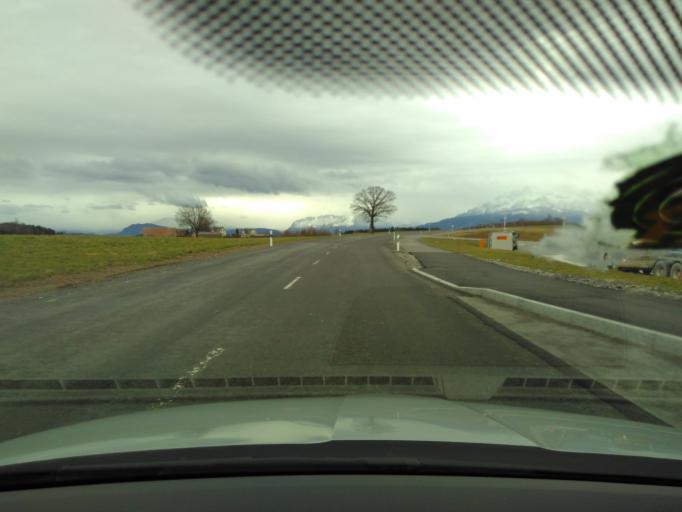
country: CH
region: Lucerne
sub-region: Sursee District
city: Hildisrieden
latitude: 47.1332
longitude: 8.2414
